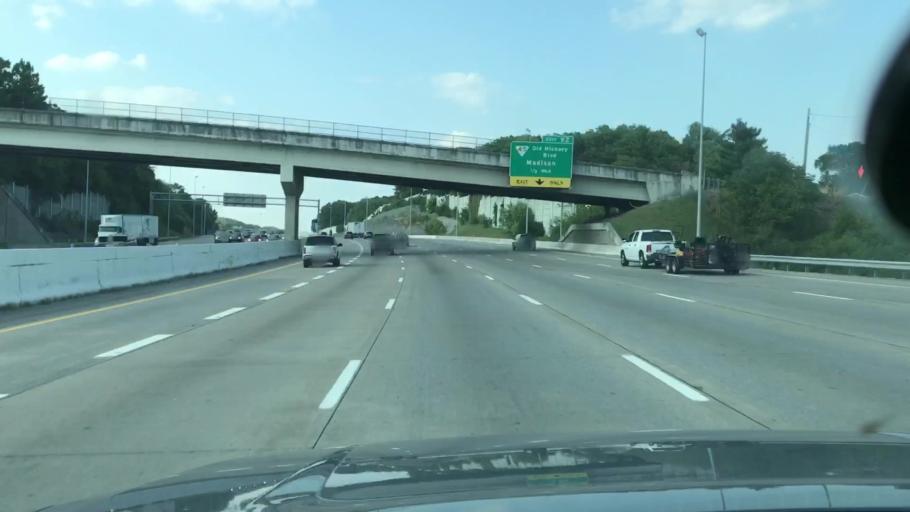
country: US
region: Tennessee
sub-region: Davidson County
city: Nashville
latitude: 36.2196
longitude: -86.8253
